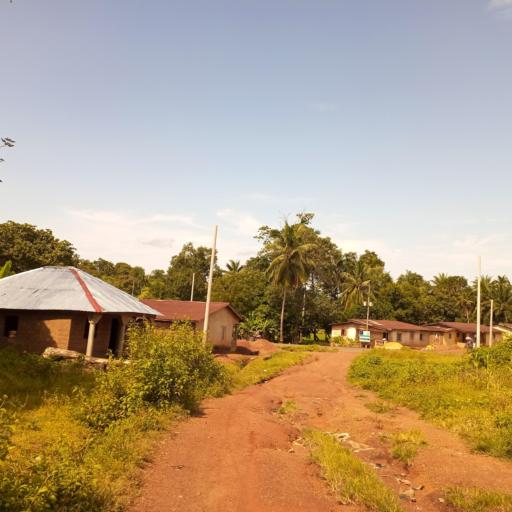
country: SL
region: Northern Province
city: Kambia
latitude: 9.1196
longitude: -12.9188
